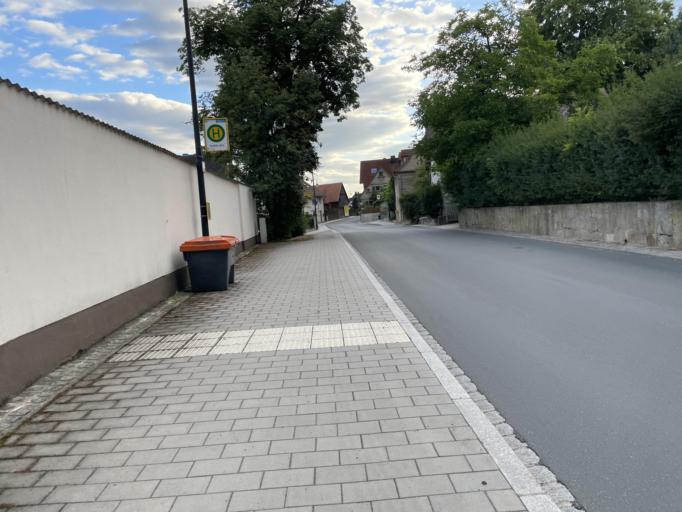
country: DE
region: Bavaria
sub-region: Upper Franconia
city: Neunkirchen am Main
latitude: 49.9420
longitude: 11.6444
